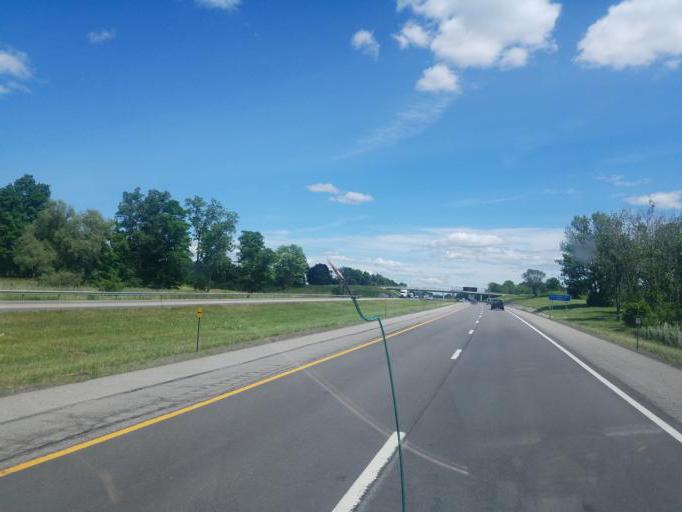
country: US
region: New York
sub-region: Monroe County
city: Pittsford
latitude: 43.0235
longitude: -77.5006
